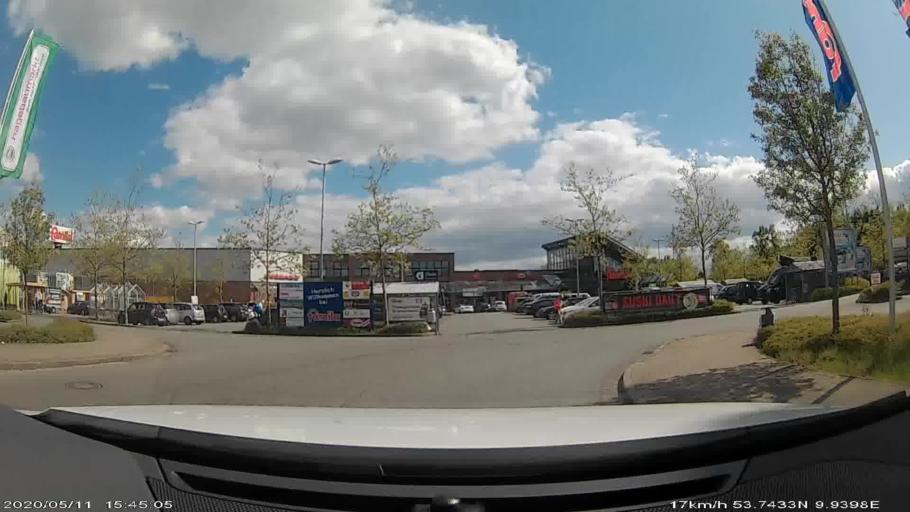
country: DE
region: Schleswig-Holstein
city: Ellerau
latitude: 53.7411
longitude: 9.9589
